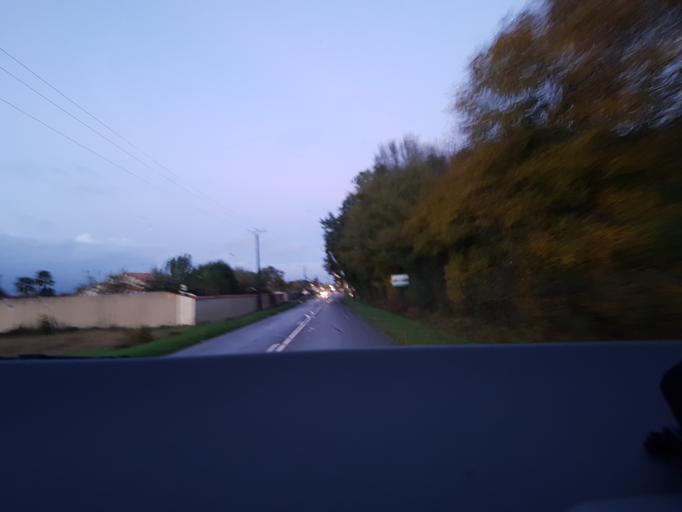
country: FR
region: Poitou-Charentes
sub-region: Departement des Deux-Sevres
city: Lezay
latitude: 46.2583
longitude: -0.0188
